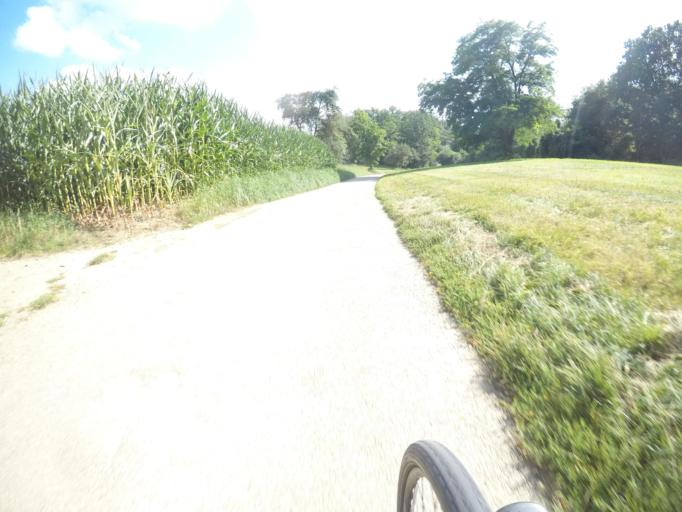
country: DE
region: Baden-Wuerttemberg
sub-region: Karlsruhe Region
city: Kieselbronn
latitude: 48.9437
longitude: 8.7719
